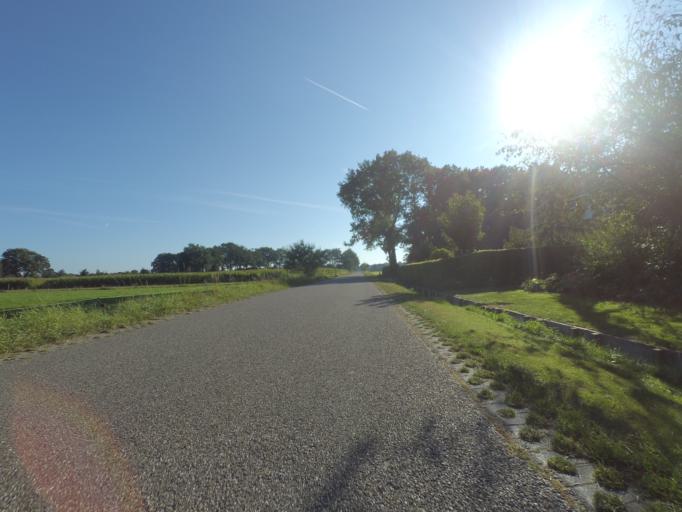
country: NL
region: Gelderland
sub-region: Gemeente Putten
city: Putten
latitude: 52.2391
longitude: 5.5869
